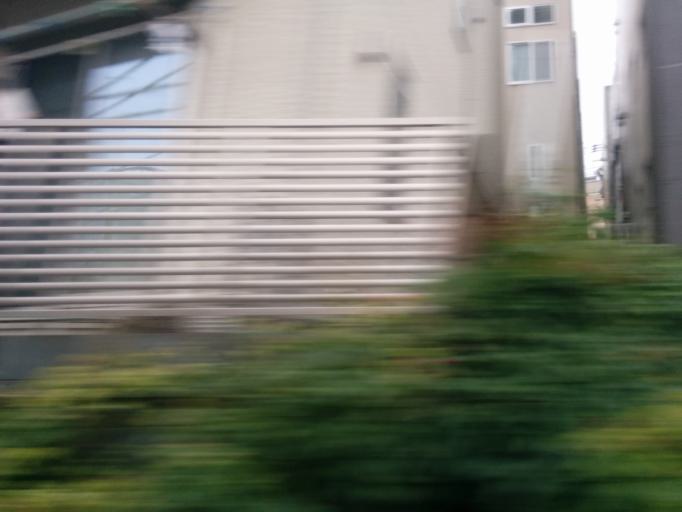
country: JP
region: Tokyo
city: Tokyo
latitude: 35.6815
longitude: 139.6959
